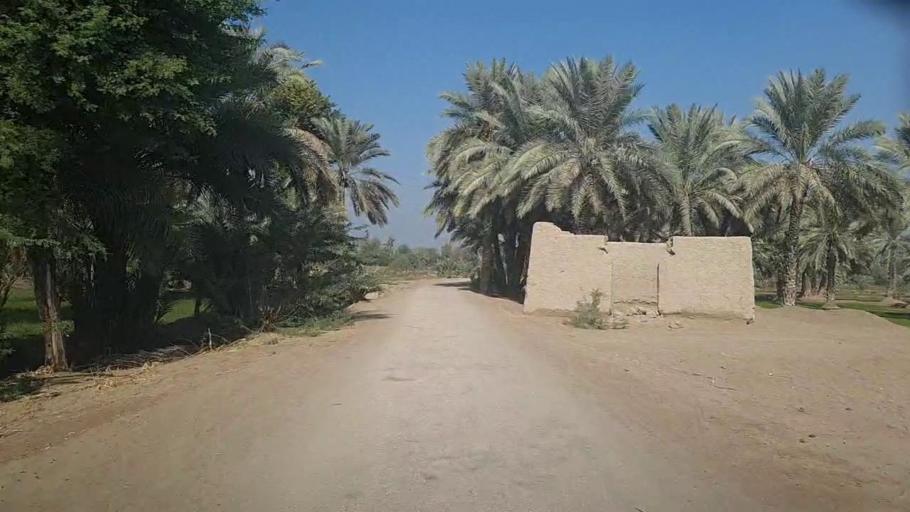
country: PK
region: Sindh
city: Kot Diji
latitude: 27.4196
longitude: 68.7060
